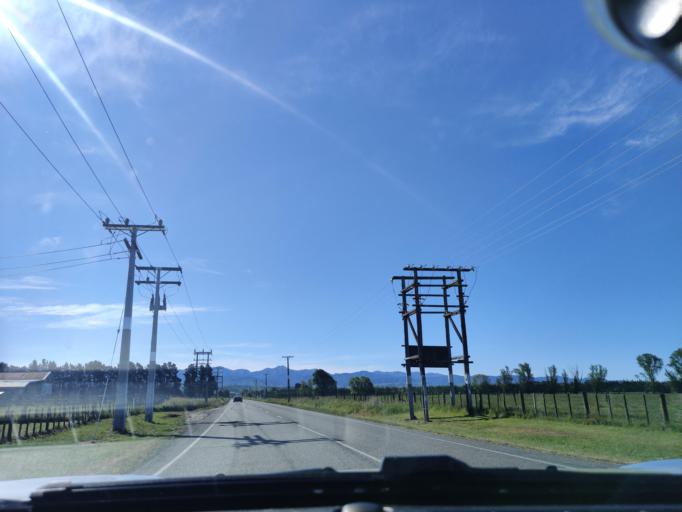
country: NZ
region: Wellington
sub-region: Masterton District
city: Masterton
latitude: -40.9363
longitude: 175.6518
